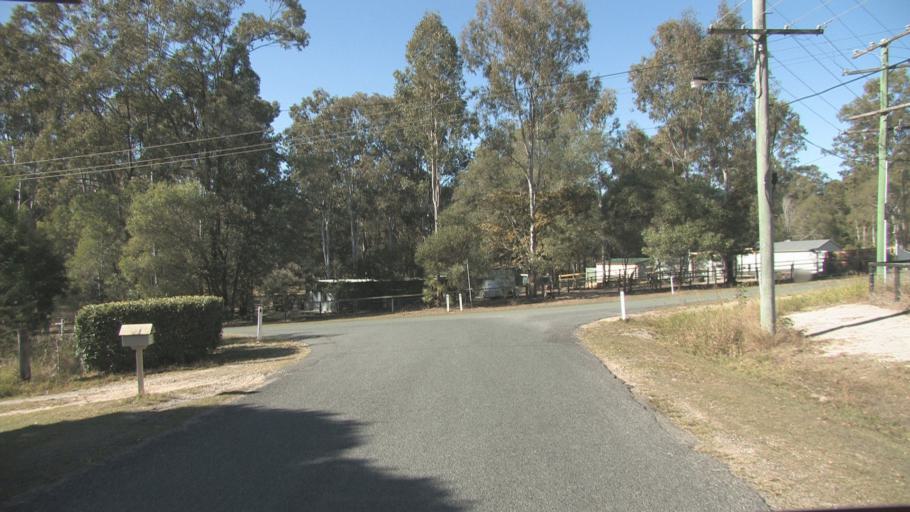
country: AU
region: Queensland
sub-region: Logan
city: Chambers Flat
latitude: -27.7878
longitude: 153.1316
